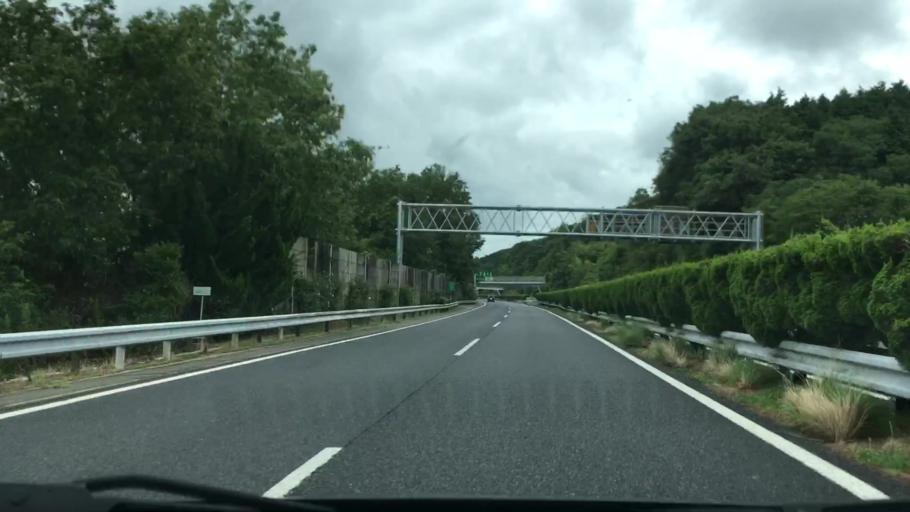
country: JP
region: Okayama
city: Tsuyama
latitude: 35.0388
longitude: 134.1284
